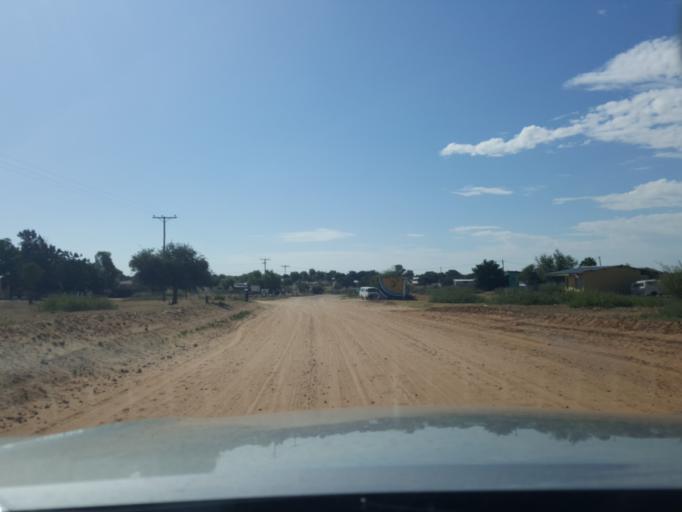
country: BW
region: Kweneng
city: Khudumelapye
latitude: -23.6976
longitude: 24.7189
